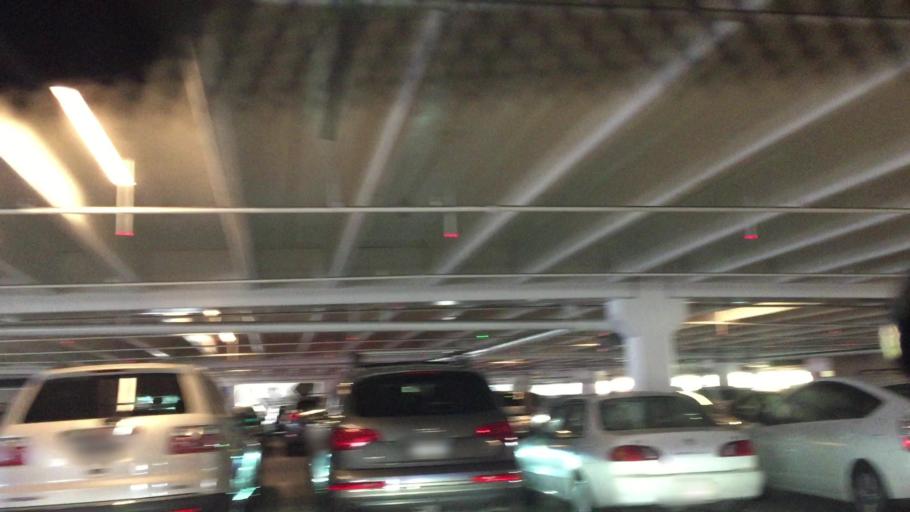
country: US
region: California
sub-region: Contra Costa County
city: Walnut Creek
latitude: 37.8944
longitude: -122.0569
